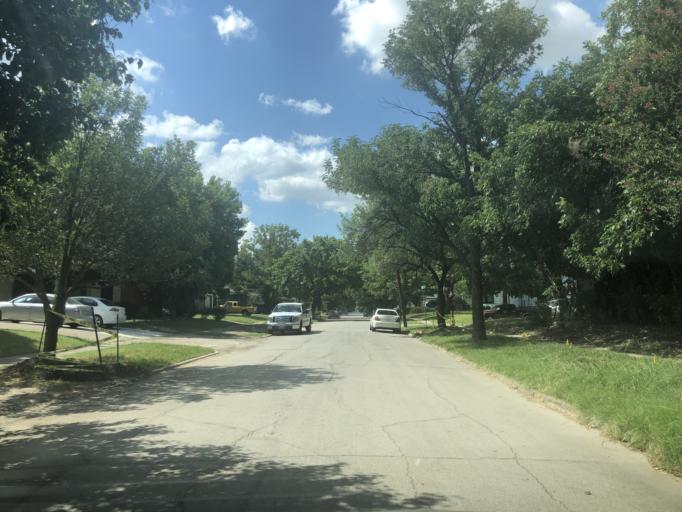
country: US
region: Texas
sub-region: Dallas County
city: Grand Prairie
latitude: 32.7353
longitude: -97.0091
